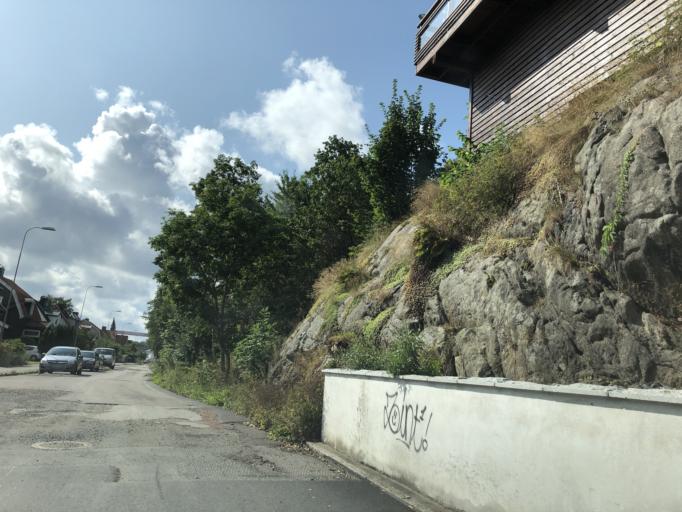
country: SE
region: Vaestra Goetaland
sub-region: Goteborg
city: Majorna
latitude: 57.7105
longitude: 11.9008
